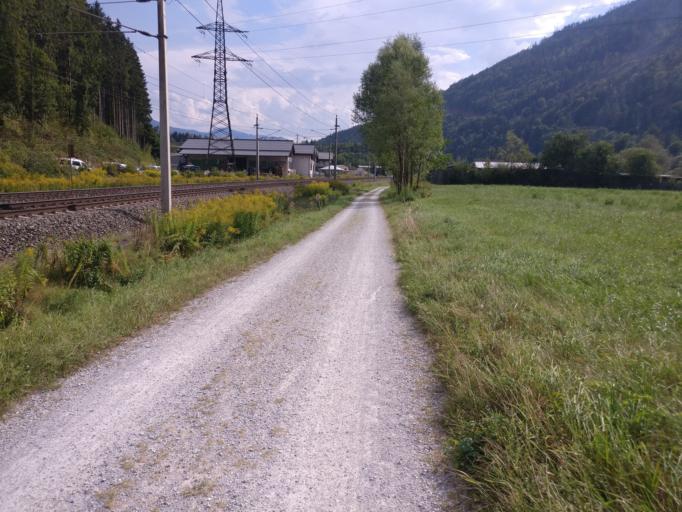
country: AT
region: Salzburg
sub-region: Politischer Bezirk Sankt Johann im Pongau
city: Pfarrwerfen
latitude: 47.4418
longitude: 13.2131
